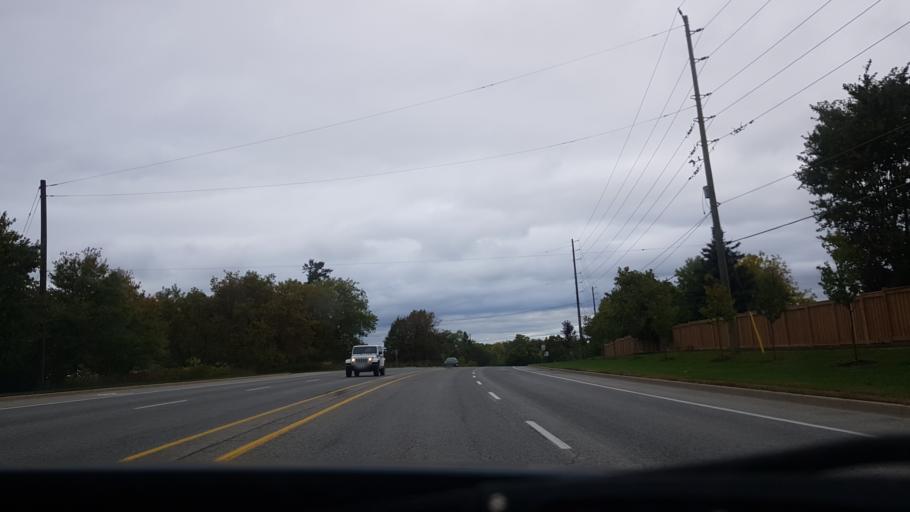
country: CA
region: Ontario
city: Newmarket
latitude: 44.0409
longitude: -79.5034
